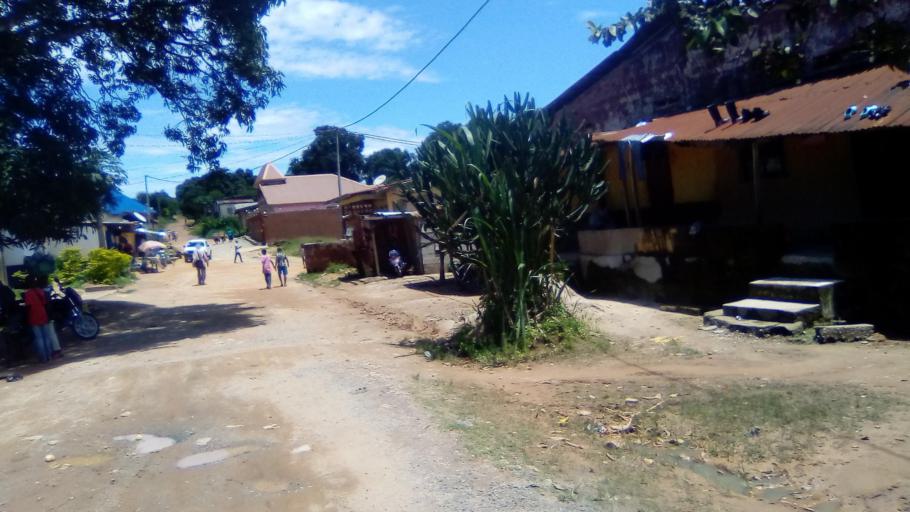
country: SL
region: Eastern Province
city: Koidu
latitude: 8.6390
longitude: -10.9827
